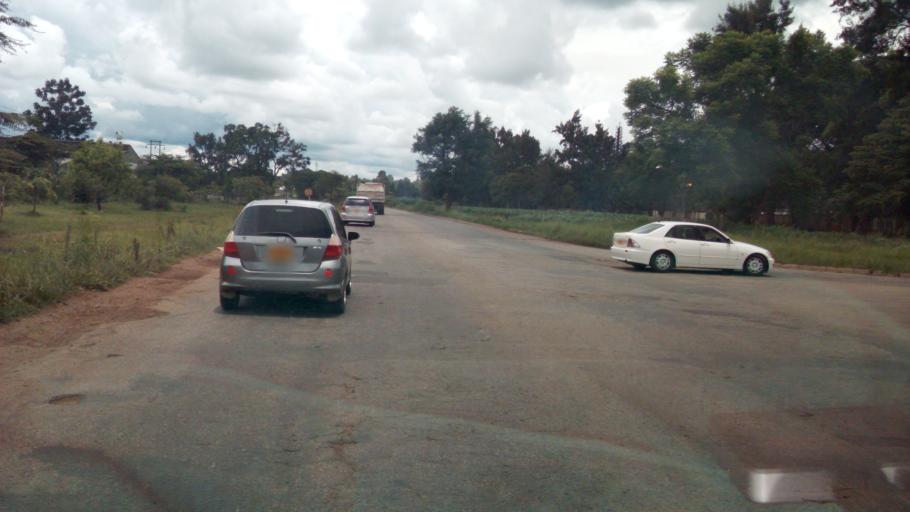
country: ZW
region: Harare
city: Harare
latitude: -17.7858
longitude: 30.9914
